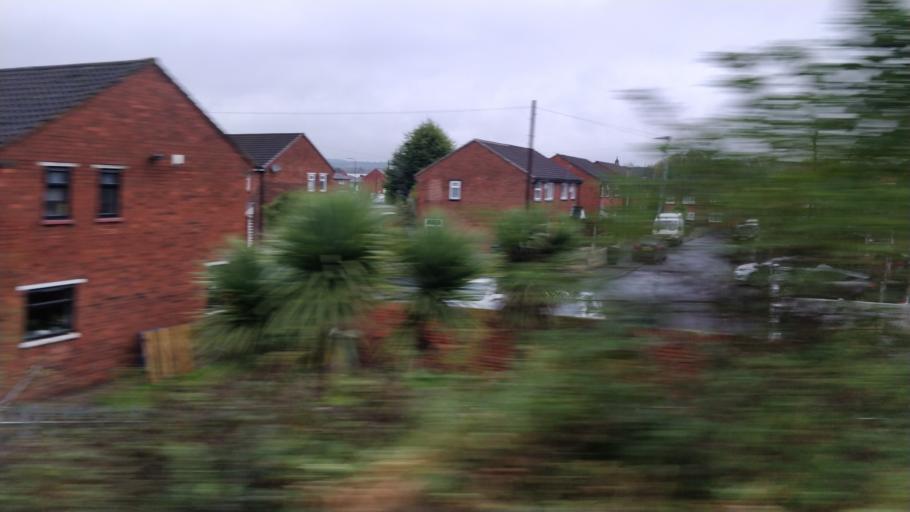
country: GB
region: England
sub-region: Borough of Wigan
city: Ince-in-Makerfield
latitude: 53.5388
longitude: -2.6096
